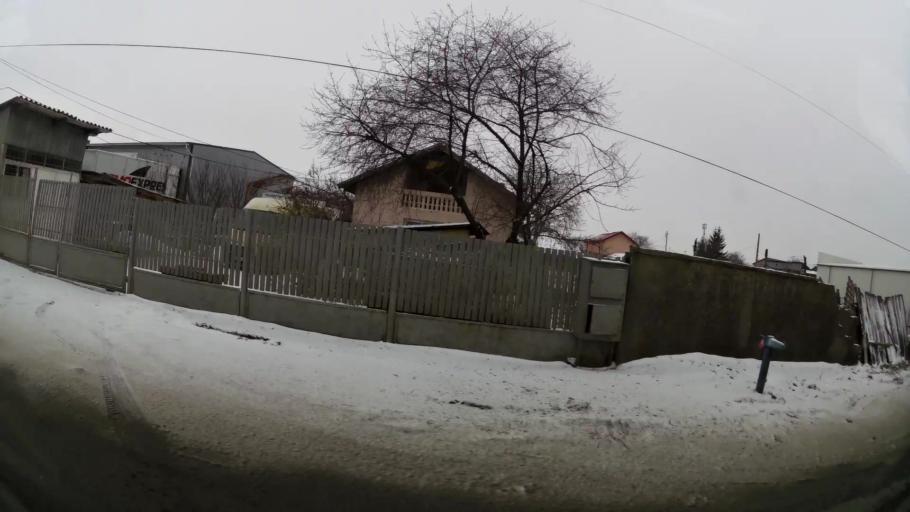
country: RO
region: Dambovita
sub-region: Comuna Ulmi
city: Ulmi
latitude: 44.9049
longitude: 25.4949
